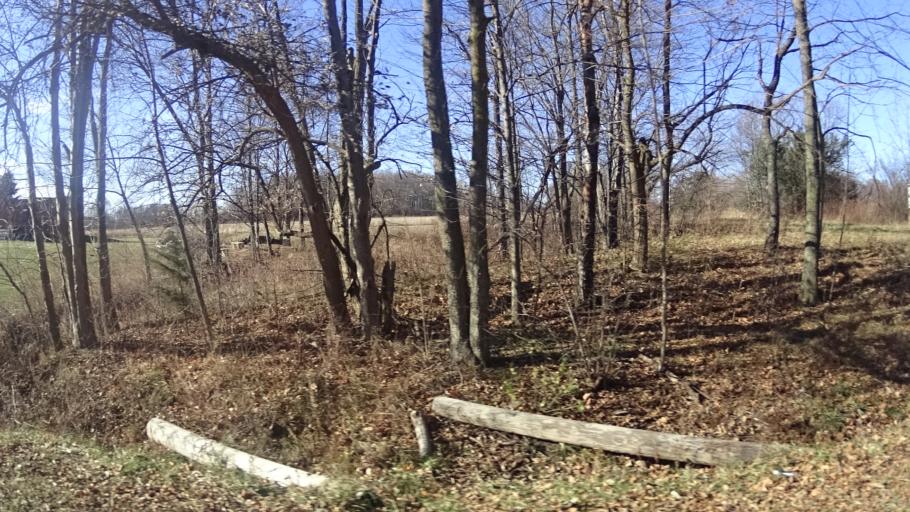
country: US
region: Ohio
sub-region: Lorain County
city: South Amherst
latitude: 41.3389
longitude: -82.2884
